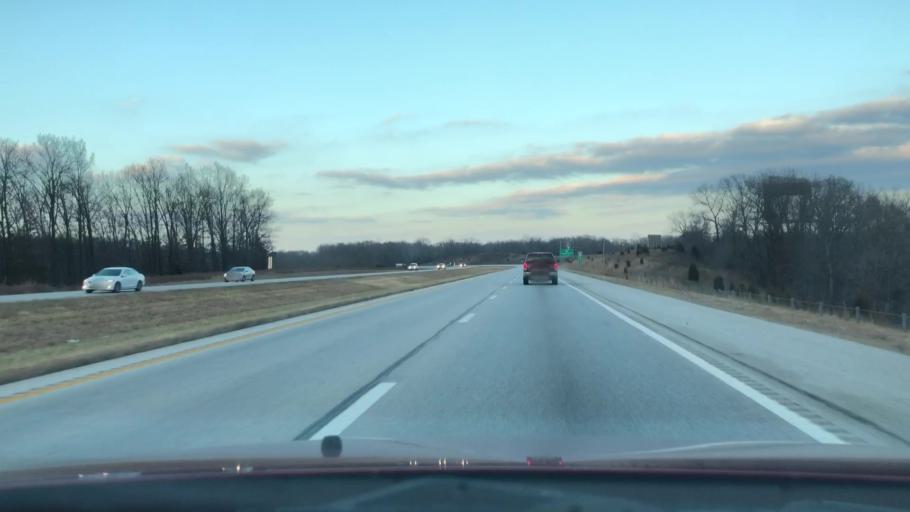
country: US
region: Missouri
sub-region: Christian County
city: Ozark
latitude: 36.9244
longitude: -93.2378
